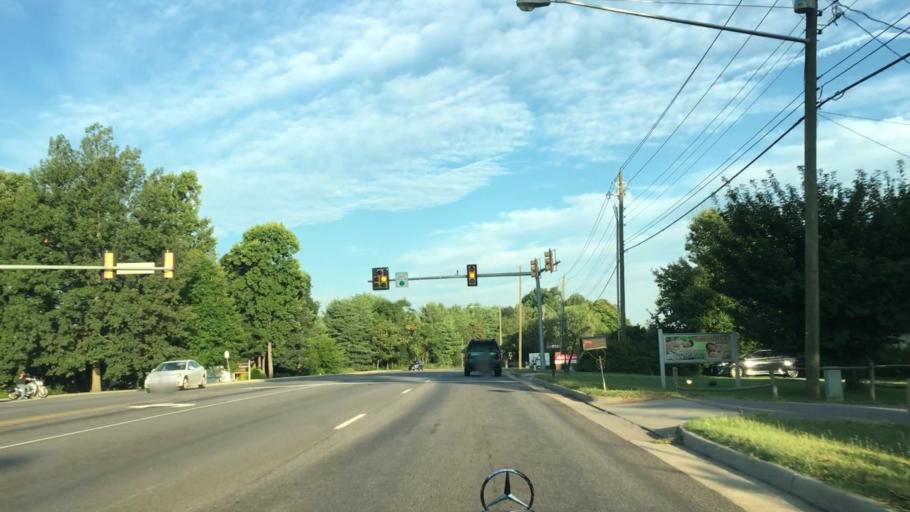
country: US
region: Virginia
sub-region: Bedford County
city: Forest
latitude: 37.3770
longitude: -79.2394
